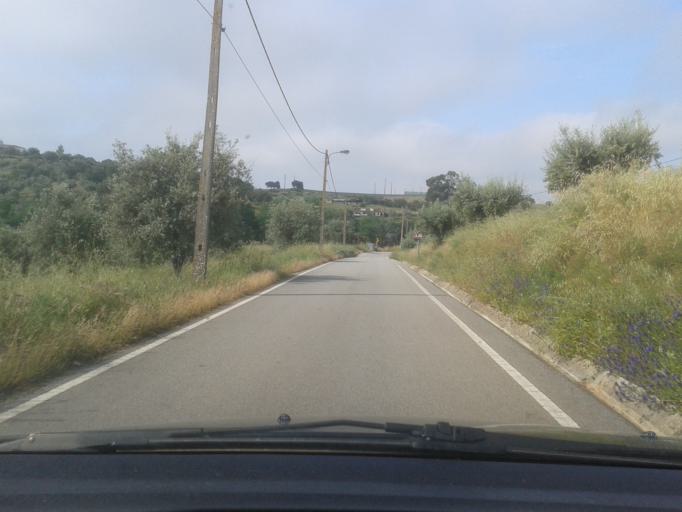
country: PT
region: Portalegre
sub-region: Avis
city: Avis
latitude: 39.0267
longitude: -7.9275
